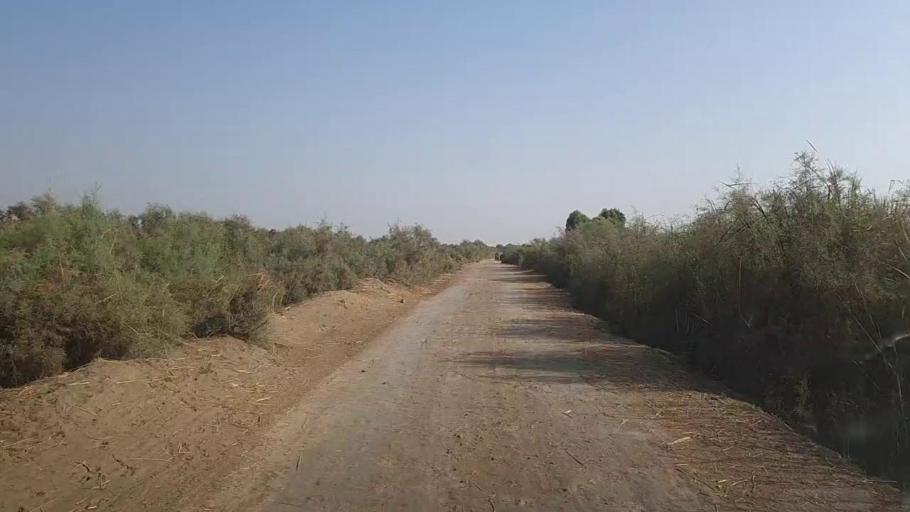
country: PK
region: Sindh
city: Kandhkot
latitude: 28.3569
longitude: 69.3336
